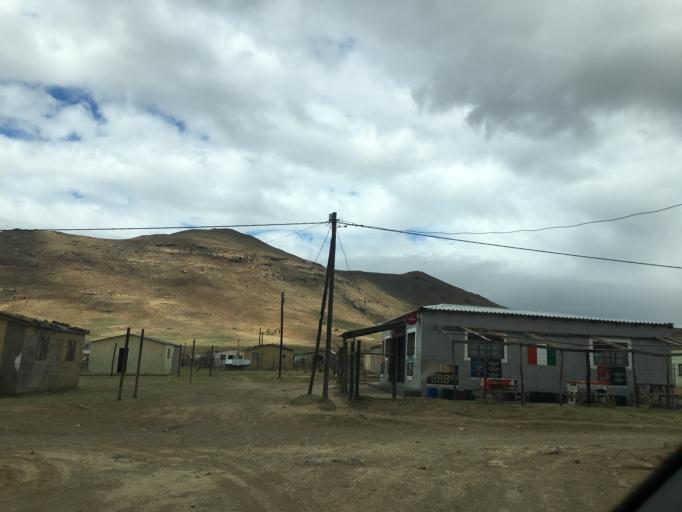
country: ZA
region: Eastern Cape
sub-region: Chris Hani District Municipality
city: Cala
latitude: -31.5405
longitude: 27.6993
